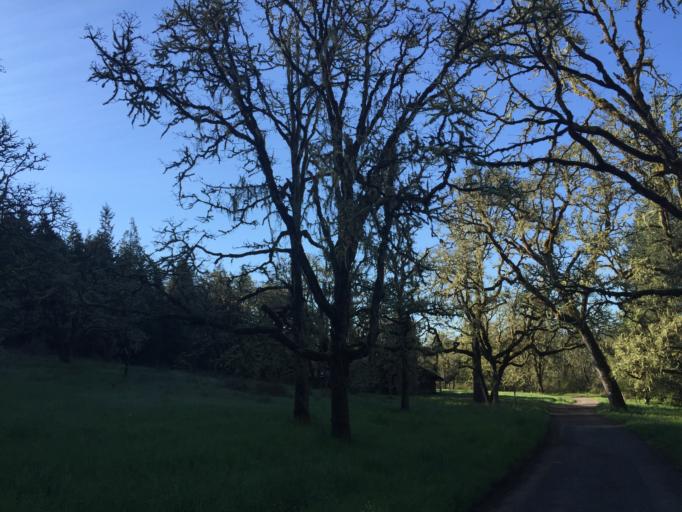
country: US
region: Oregon
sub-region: Lane County
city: Springfield
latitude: 44.0043
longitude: -122.9805
